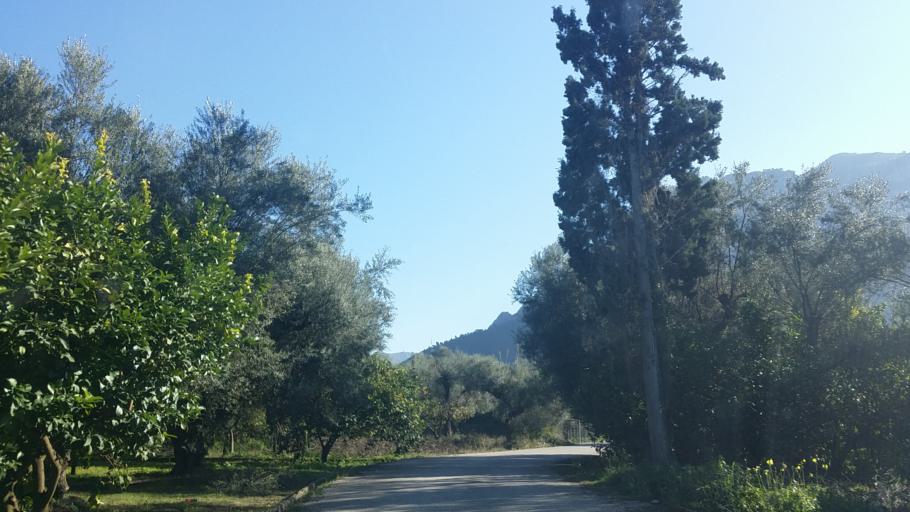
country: GR
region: West Greece
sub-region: Nomos Achaias
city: Temeni
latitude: 38.1894
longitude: 22.1889
